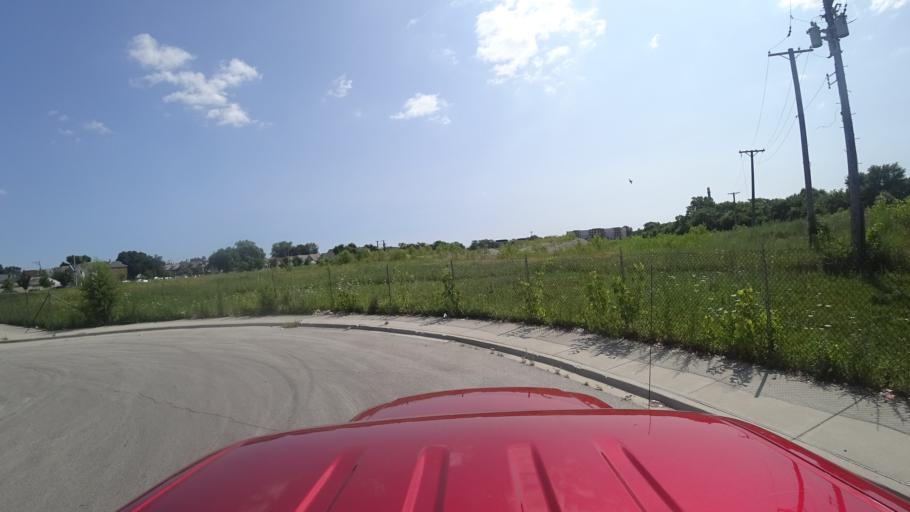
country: US
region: Illinois
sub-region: Cook County
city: Chicago
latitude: 41.8055
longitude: -87.6892
